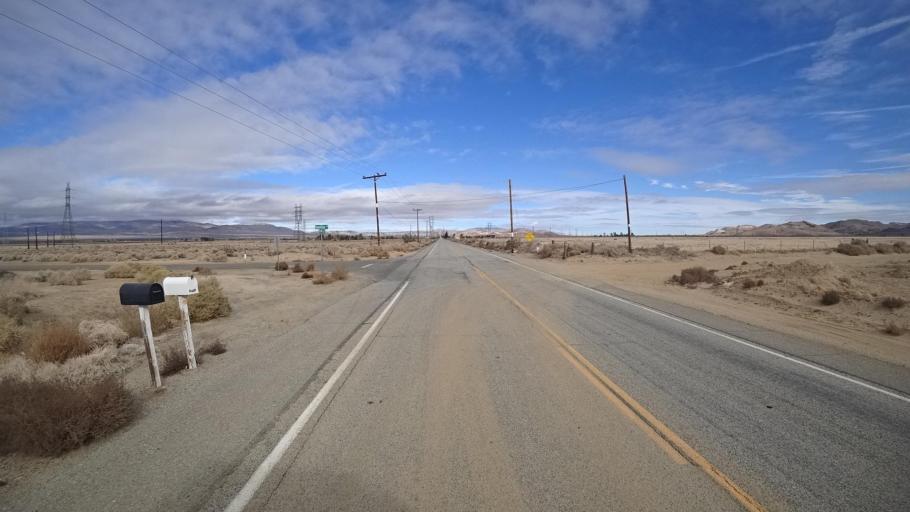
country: US
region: California
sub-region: Kern County
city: Rosamond
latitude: 34.8925
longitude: -118.2911
